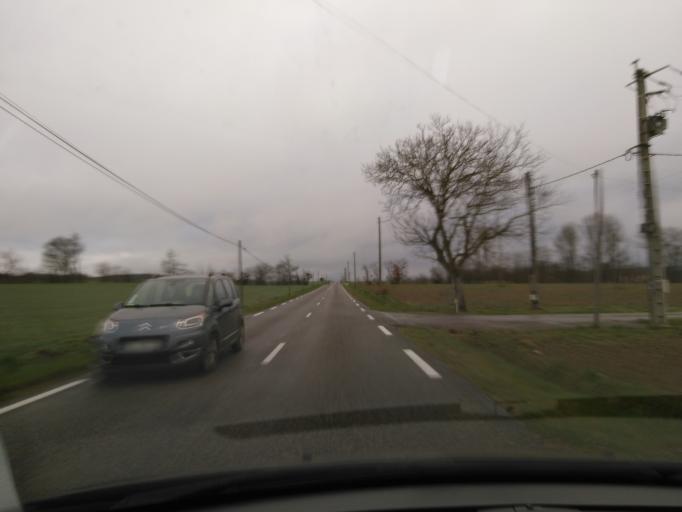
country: FR
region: Midi-Pyrenees
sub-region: Departement de la Haute-Garonne
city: Montesquieu-Volvestre
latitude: 43.1721
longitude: 1.2602
